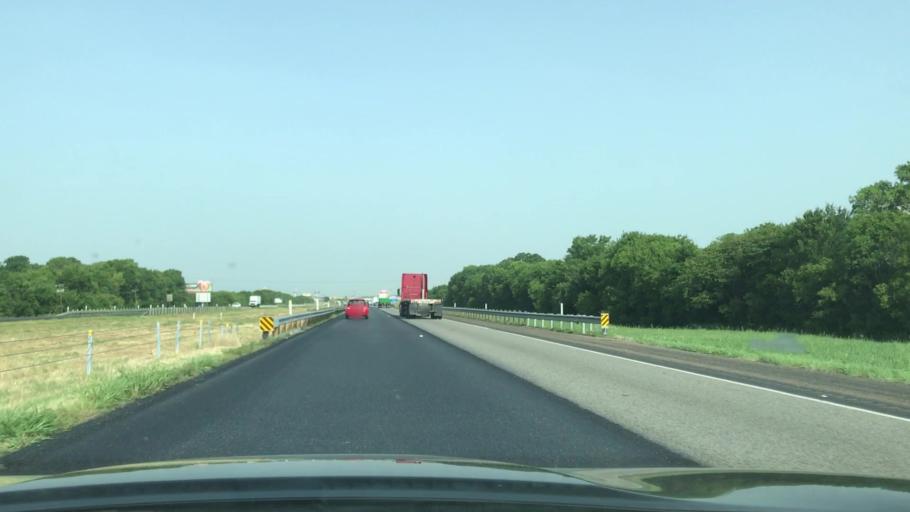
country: US
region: Texas
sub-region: Kaufman County
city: Terrell
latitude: 32.6971
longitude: -96.2592
